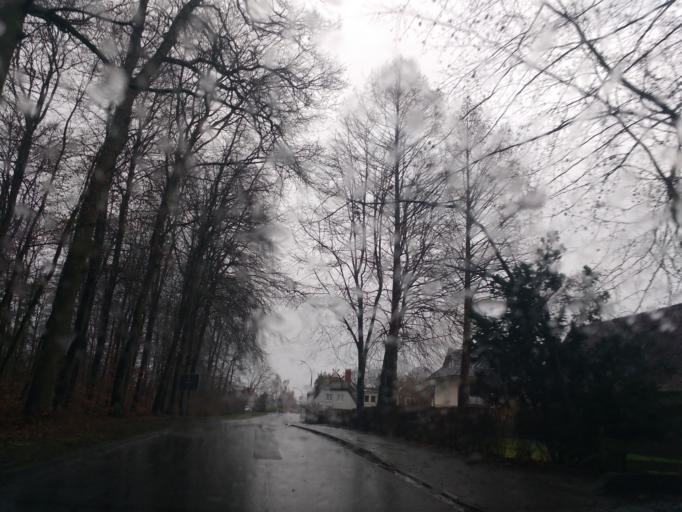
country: DE
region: Schleswig-Holstein
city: Blekendorf
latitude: 54.3215
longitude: 10.6619
